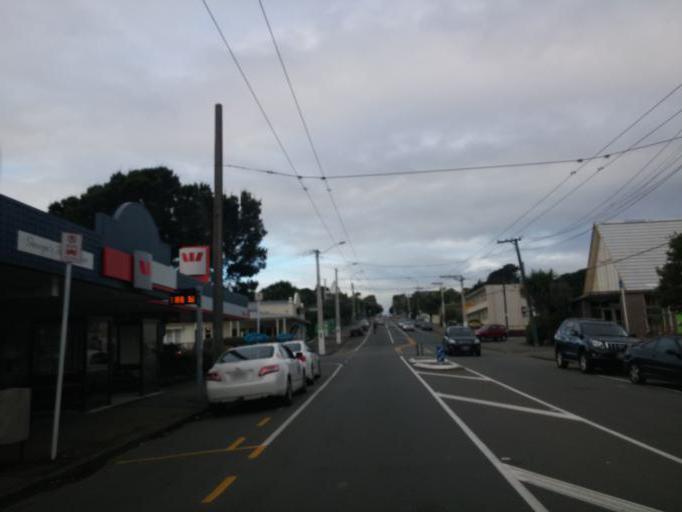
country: NZ
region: Wellington
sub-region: Wellington City
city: Kelburn
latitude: -41.2845
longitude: 174.7381
